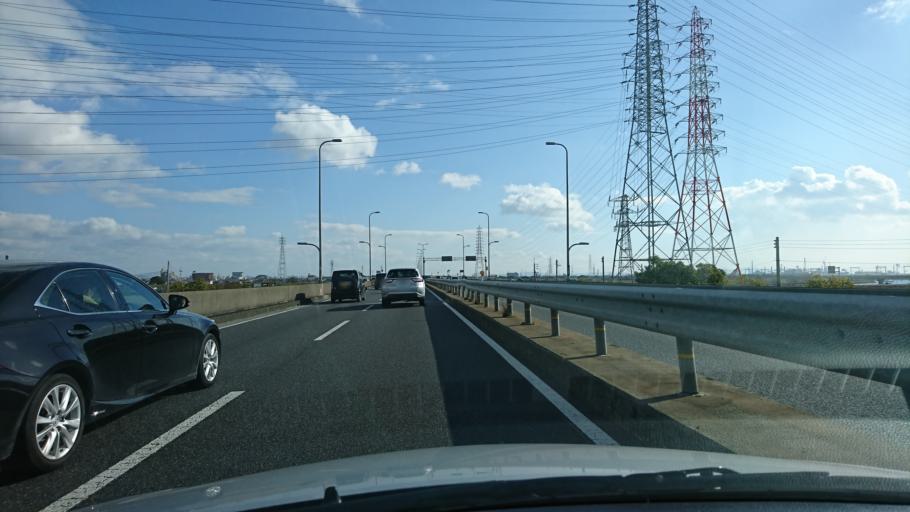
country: JP
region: Hyogo
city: Kakogawacho-honmachi
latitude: 34.7678
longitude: 134.8065
